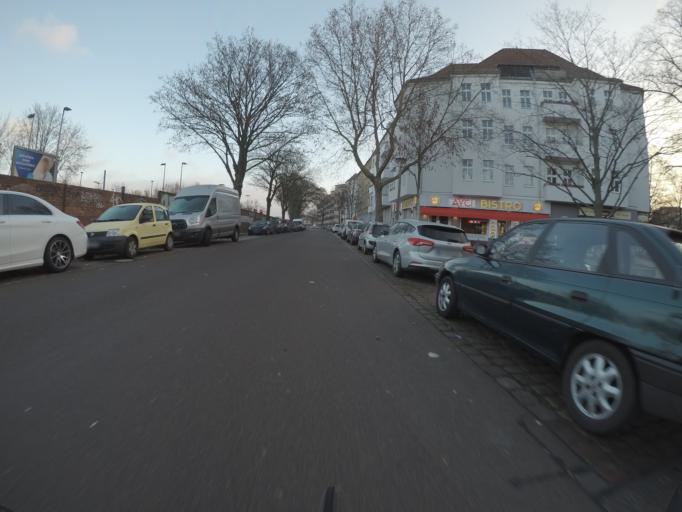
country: DE
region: Berlin
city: Rummelsburg
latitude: 52.5037
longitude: 13.4855
